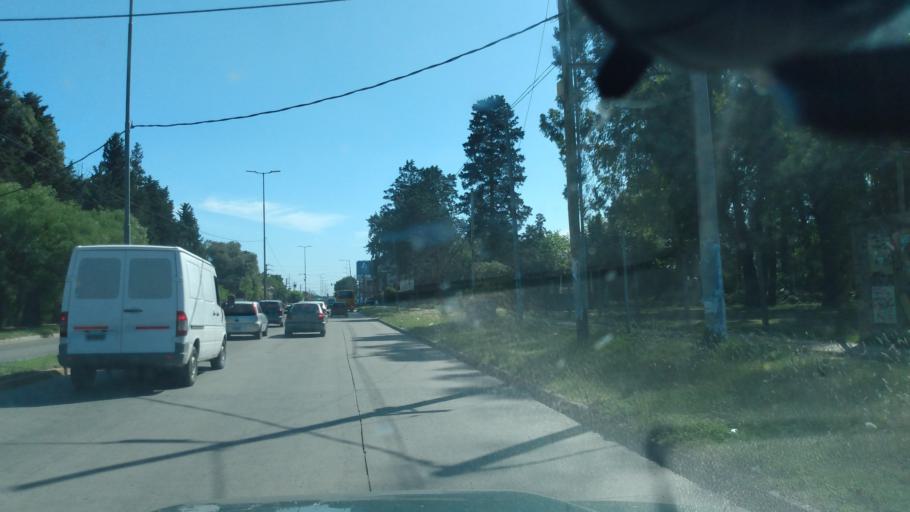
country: AR
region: Buenos Aires
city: Hurlingham
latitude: -34.5592
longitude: -58.7310
